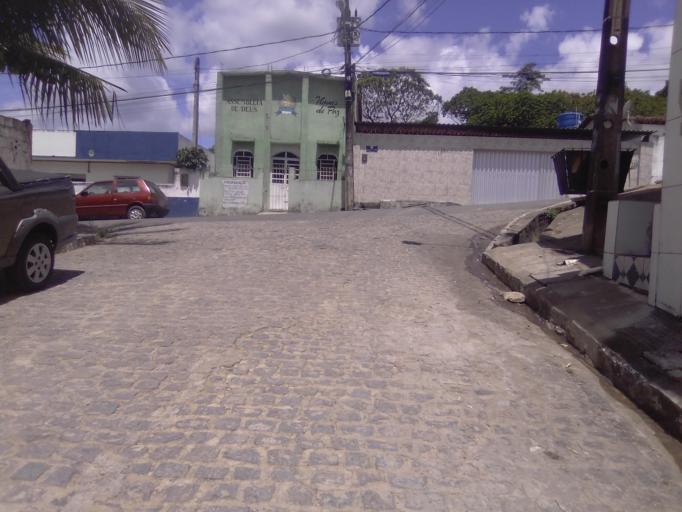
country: BR
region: Pernambuco
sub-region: Jaboatao Dos Guararapes
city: Jaboatao dos Guararapes
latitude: -8.0653
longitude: -35.0002
